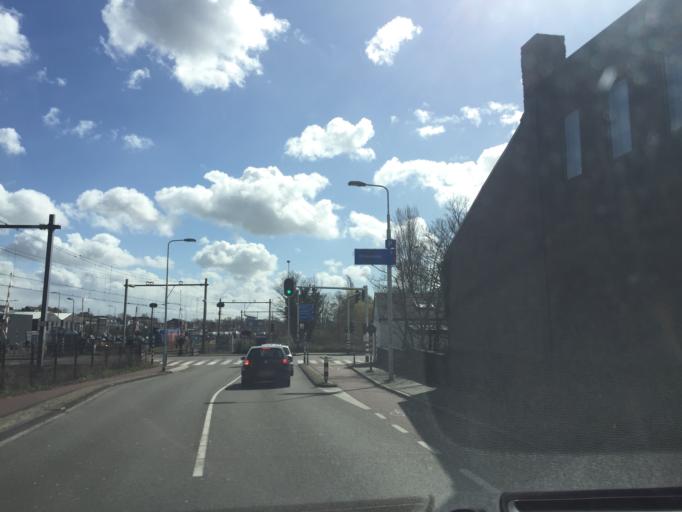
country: NL
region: South Holland
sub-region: Gemeente Leiden
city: Leiden
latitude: 52.1600
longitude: 4.4775
